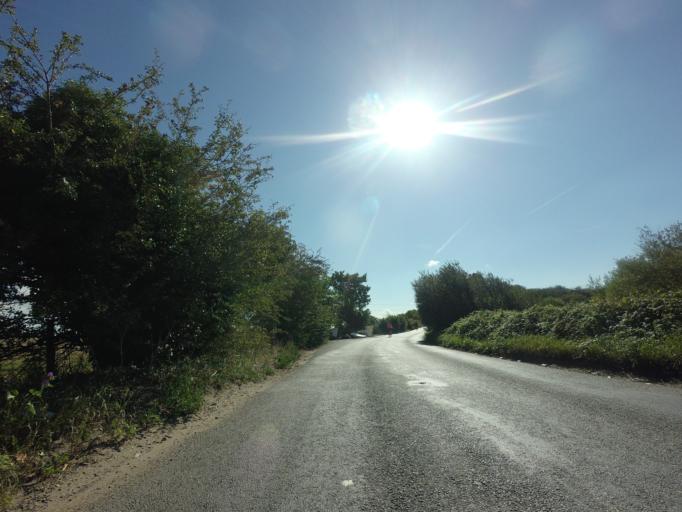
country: GB
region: England
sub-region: Kent
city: Gravesend
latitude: 51.4321
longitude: 0.4226
